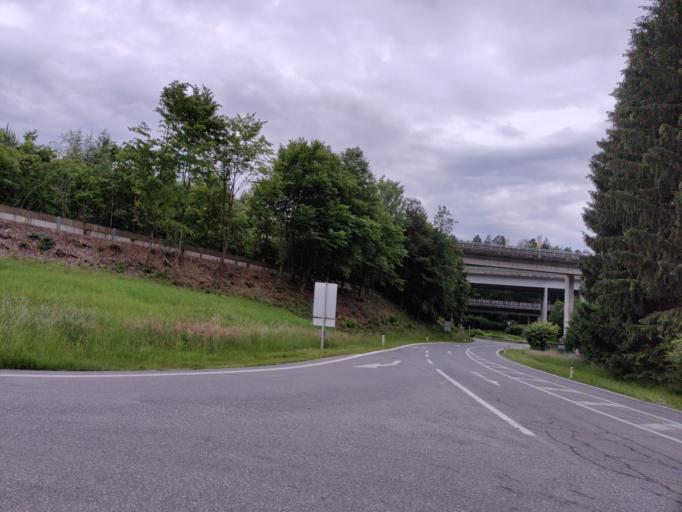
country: AT
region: Carinthia
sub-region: Politischer Bezirk Klagenfurt Land
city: Keutschach am See
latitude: 46.6321
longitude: 14.2389
